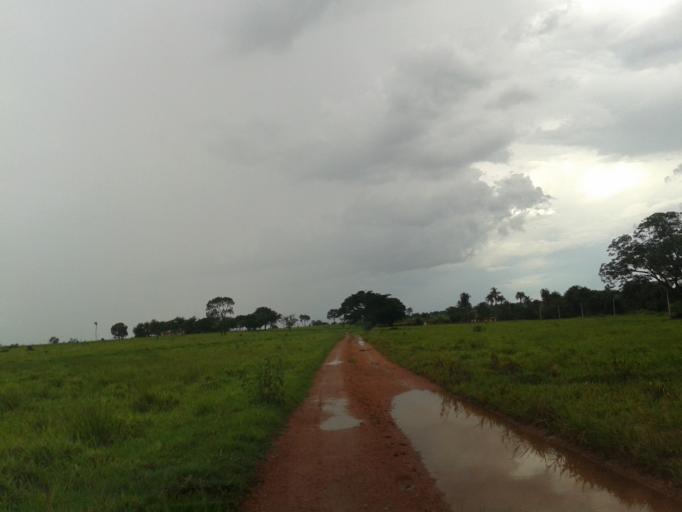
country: BR
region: Minas Gerais
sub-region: Santa Vitoria
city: Santa Vitoria
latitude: -19.1502
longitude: -50.5683
